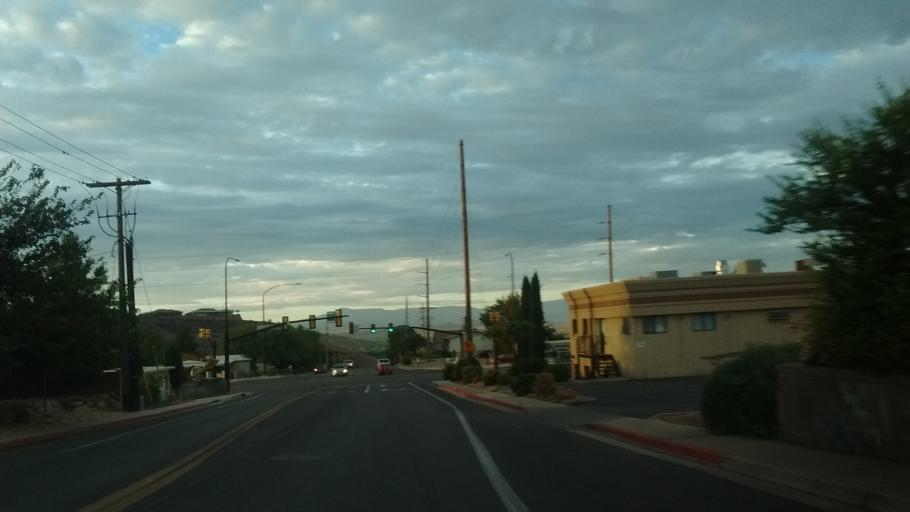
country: US
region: Utah
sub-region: Washington County
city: Washington
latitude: 37.1311
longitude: -113.5049
